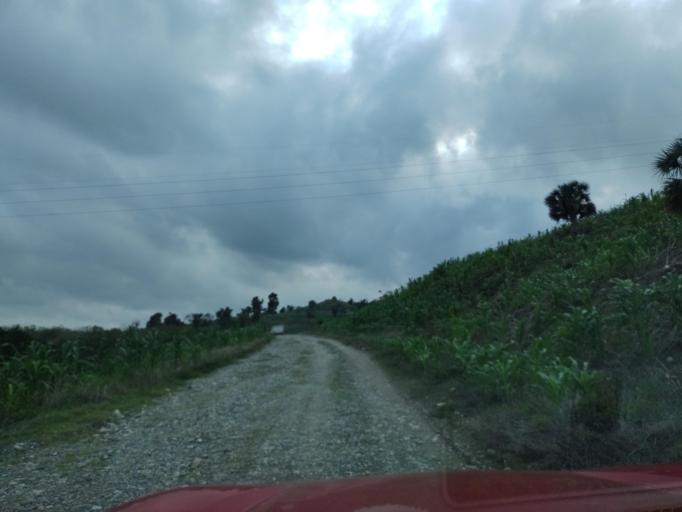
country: MX
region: Veracruz
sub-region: Papantla
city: El Chote
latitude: 20.4406
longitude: -97.4052
